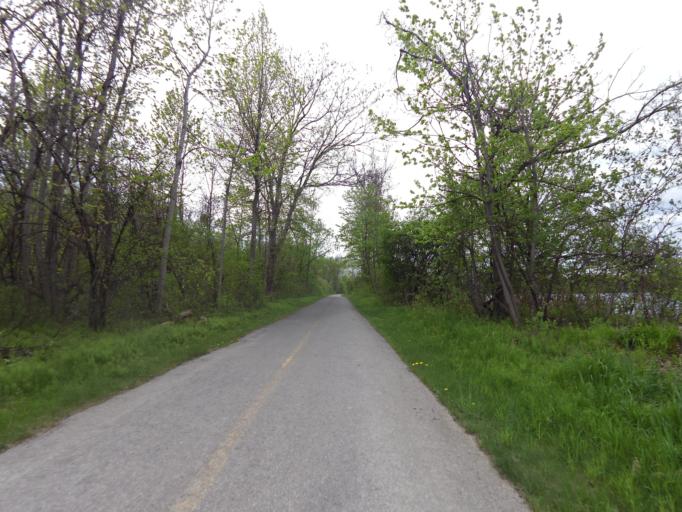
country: CA
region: Quebec
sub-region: Outaouais
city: Gatineau
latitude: 45.4567
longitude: -75.7210
